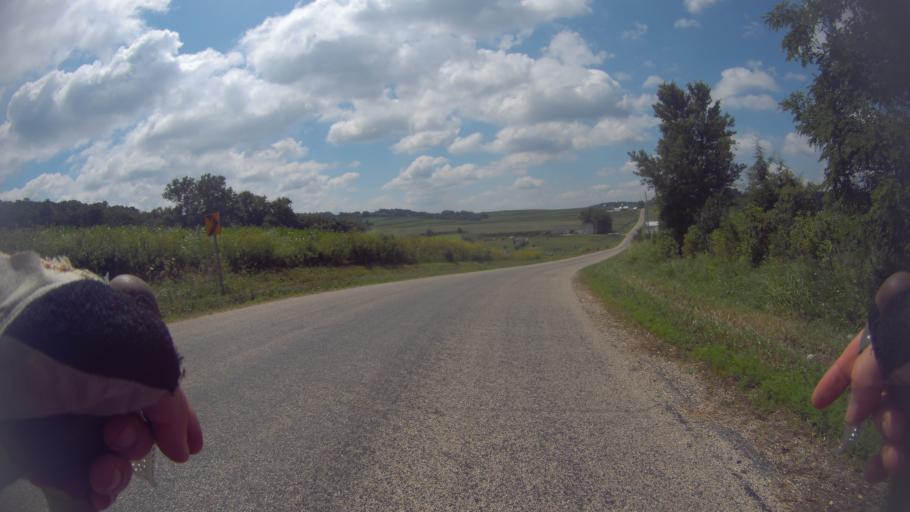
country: US
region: Wisconsin
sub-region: Sauk County
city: Sauk City
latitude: 43.2419
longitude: -89.6353
